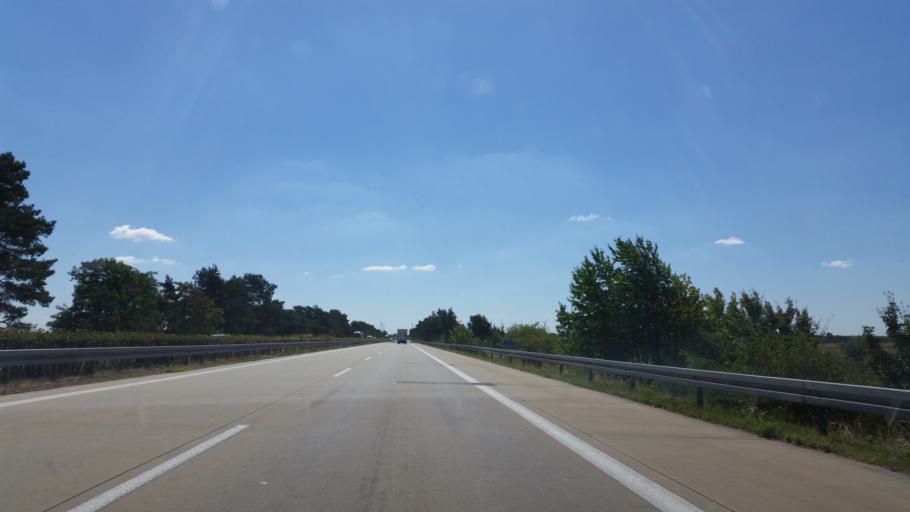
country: DE
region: Brandenburg
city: Vetschau
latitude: 51.8066
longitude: 14.0349
